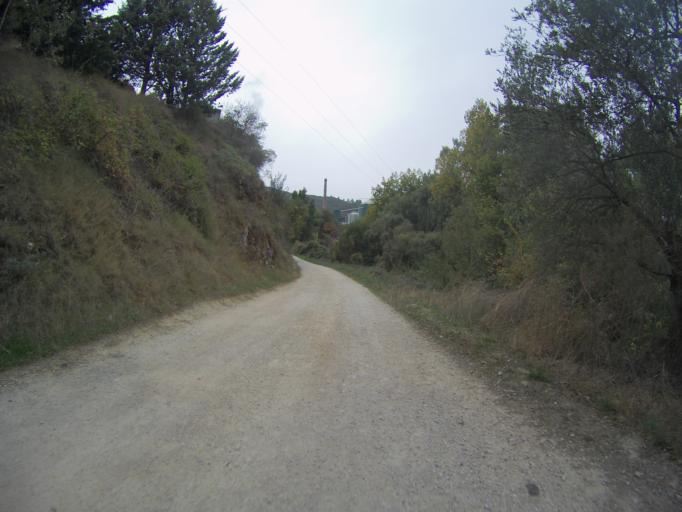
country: ES
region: Navarre
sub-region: Provincia de Navarra
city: Estella
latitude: 42.6629
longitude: -2.0172
